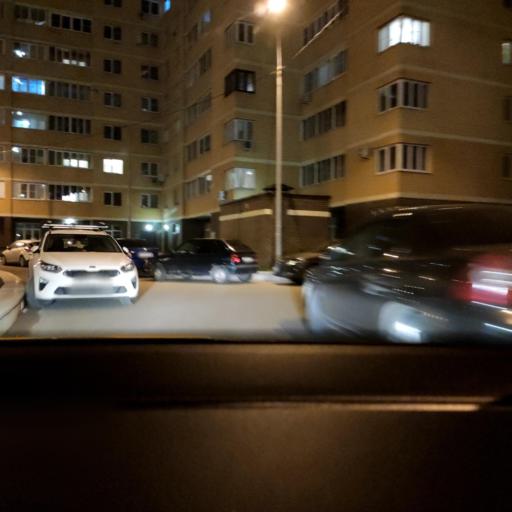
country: RU
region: Moskovskaya
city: Dolgoprudnyy
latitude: 55.9625
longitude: 37.5255
